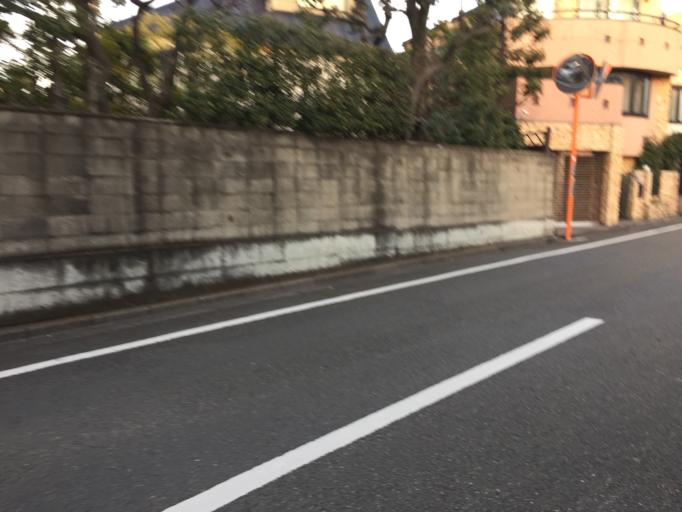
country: JP
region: Tokyo
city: Tokyo
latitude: 35.6353
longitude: 139.6487
